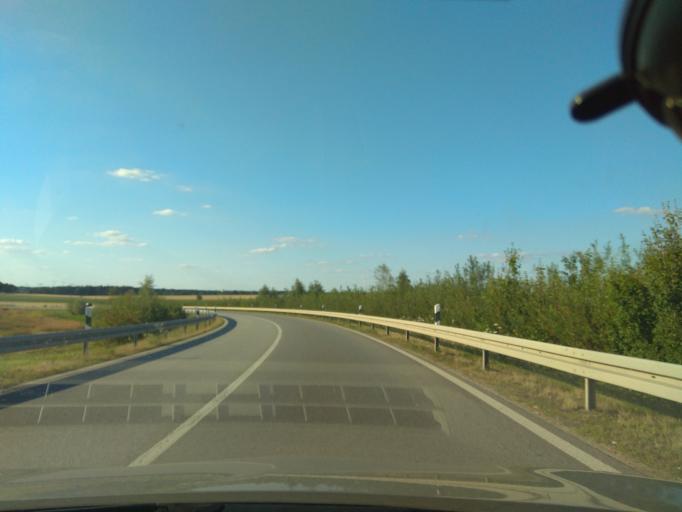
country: DE
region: Brandenburg
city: Mittenwalde
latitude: 52.2471
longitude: 13.5917
